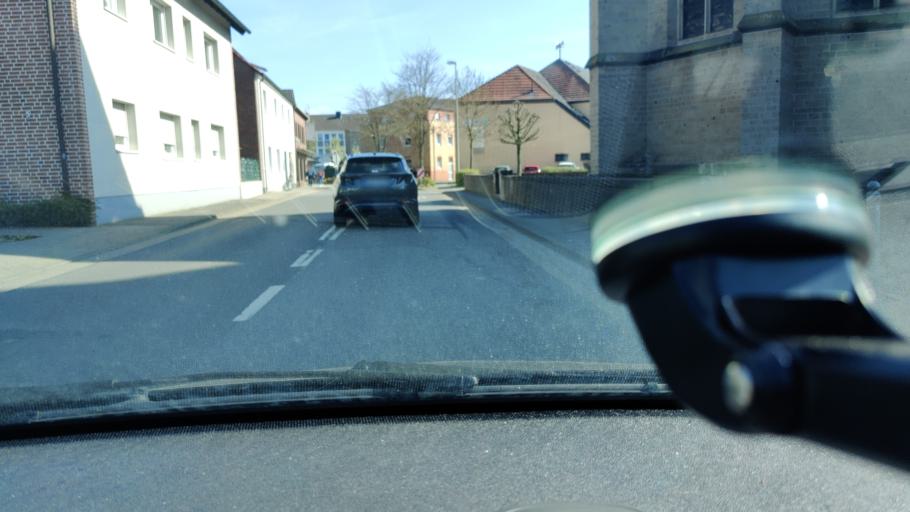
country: DE
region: North Rhine-Westphalia
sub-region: Regierungsbezirk Dusseldorf
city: Wesel
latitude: 51.6102
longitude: 6.6139
